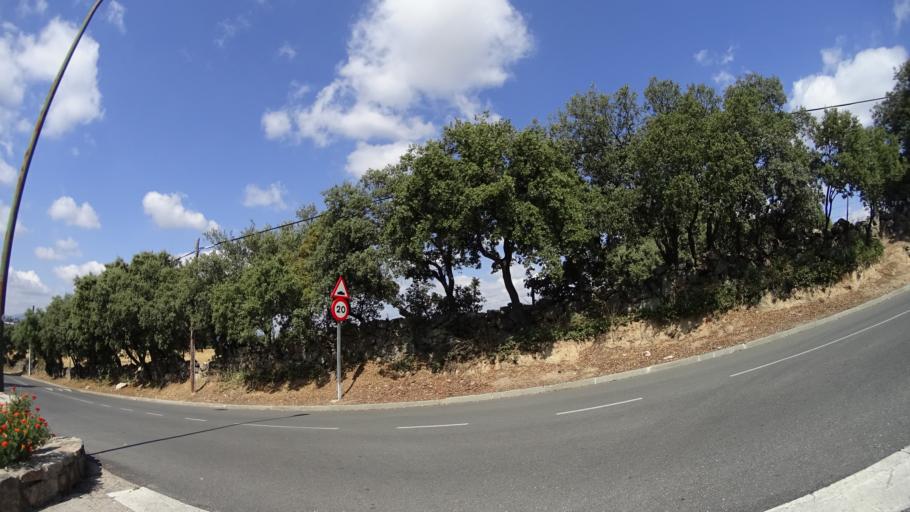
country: ES
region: Madrid
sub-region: Provincia de Madrid
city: Galapagar
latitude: 40.5836
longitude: -3.9907
